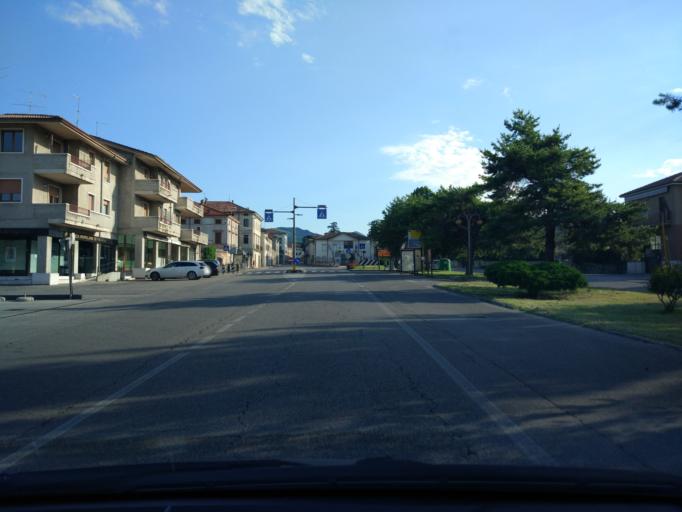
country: IT
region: Veneto
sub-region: Provincia di Verona
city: Illasi
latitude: 45.4648
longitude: 11.1793
